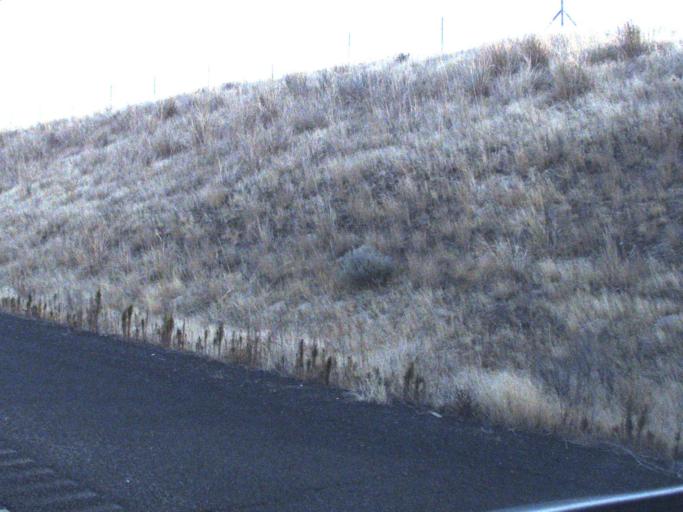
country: US
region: Washington
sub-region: Franklin County
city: Connell
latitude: 46.8657
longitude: -118.6320
